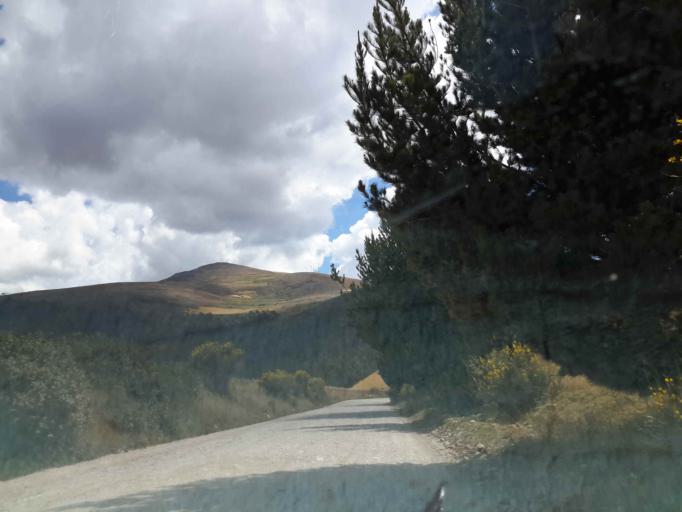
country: PE
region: Apurimac
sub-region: Provincia de Andahuaylas
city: Pacucha
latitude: -13.6334
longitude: -73.3433
